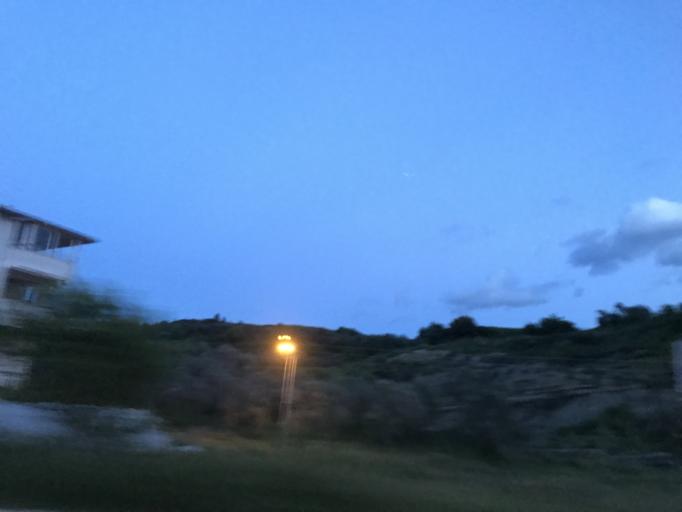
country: TR
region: Hatay
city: Samankaya
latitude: 36.1627
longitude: 36.1003
